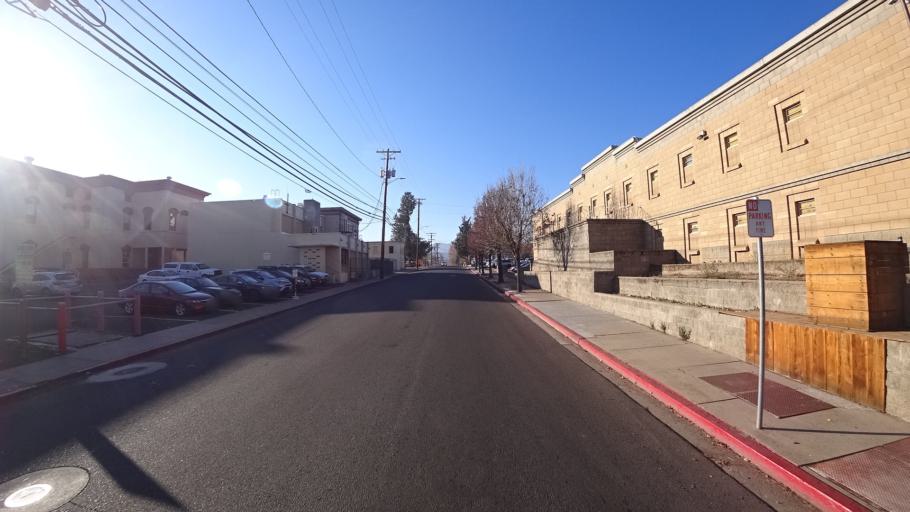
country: US
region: California
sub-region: Siskiyou County
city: Yreka
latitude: 41.7307
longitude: -122.6389
